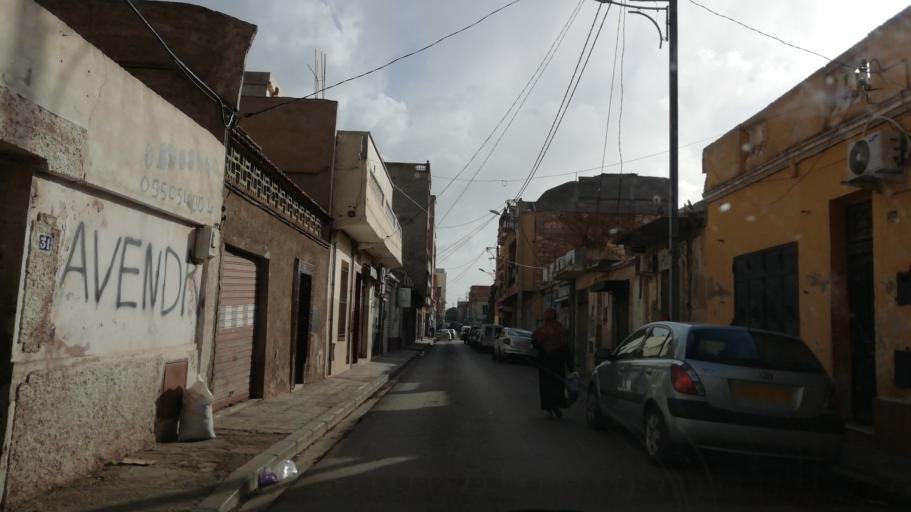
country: DZ
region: Oran
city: Oran
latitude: 35.6956
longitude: -0.6251
